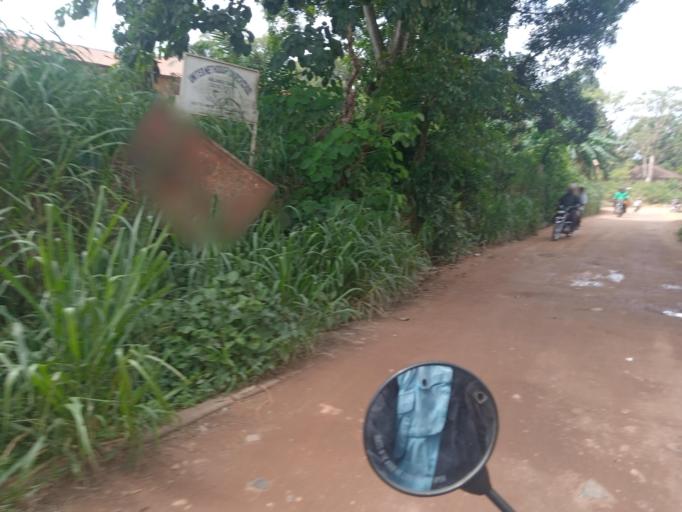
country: SL
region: Southern Province
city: Bo
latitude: 7.9757
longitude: -11.7392
